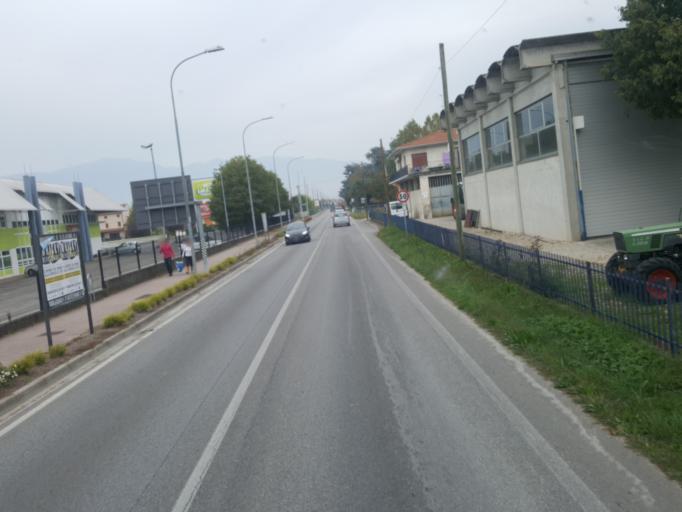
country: IT
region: Veneto
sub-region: Provincia di Treviso
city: Loria Bessica
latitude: 45.7333
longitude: 11.8665
